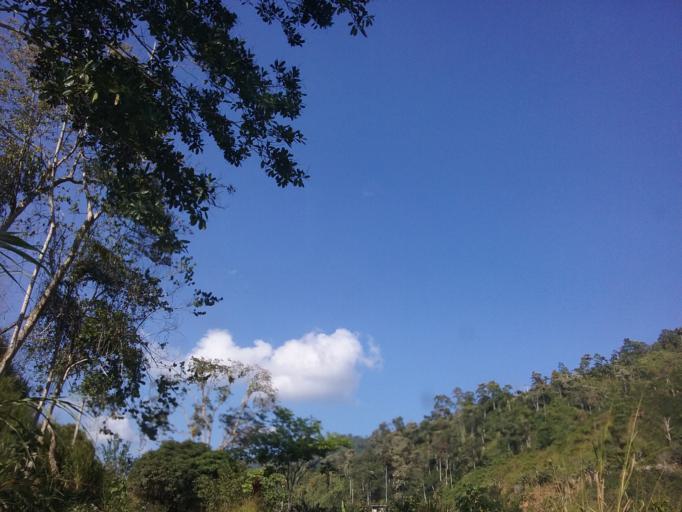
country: CO
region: Tolima
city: Libano
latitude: 4.8794
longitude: -75.0137
